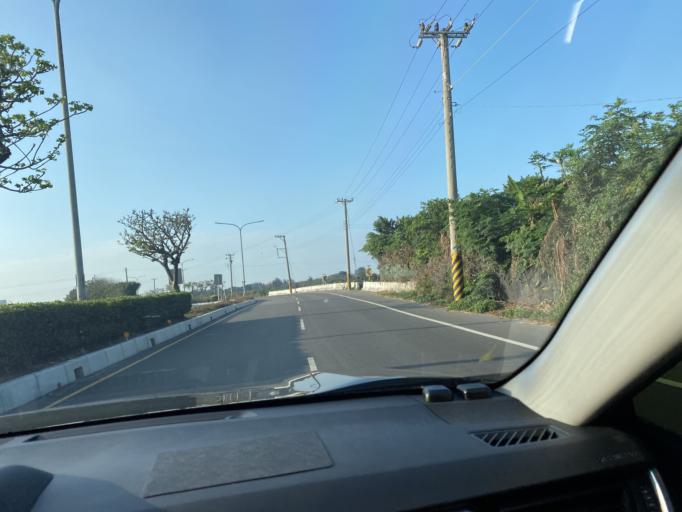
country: TW
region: Taiwan
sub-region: Changhua
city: Chang-hua
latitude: 23.9620
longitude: 120.3511
